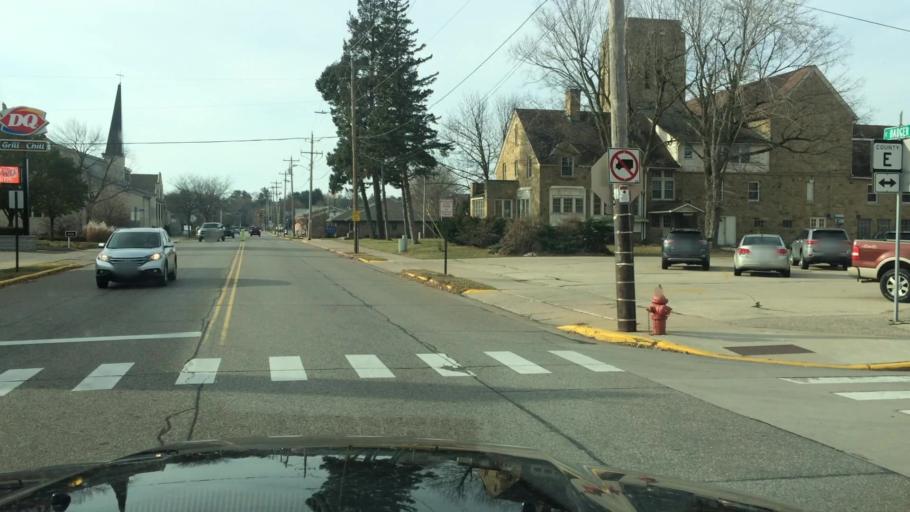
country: US
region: Wisconsin
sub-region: Waupaca County
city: Waupaca
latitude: 44.3560
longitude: -89.0811
